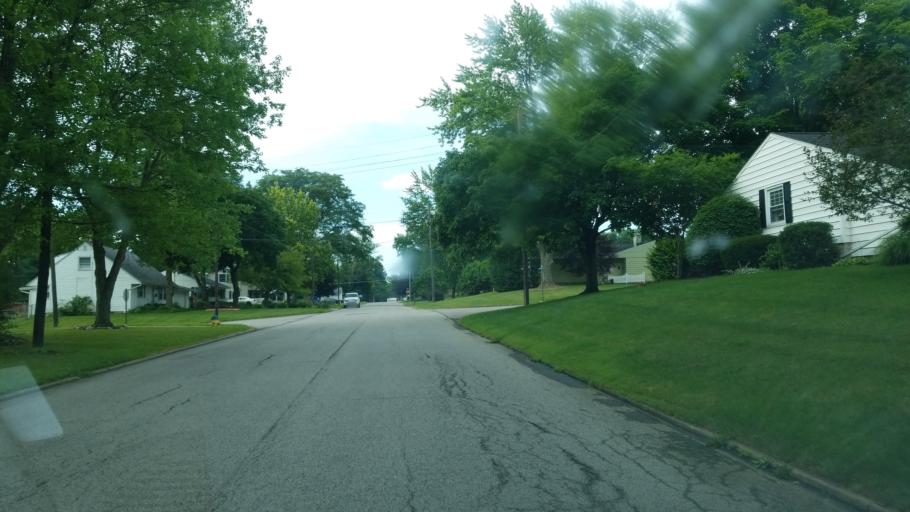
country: US
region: Ohio
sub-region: Ashland County
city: Ashland
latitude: 40.8599
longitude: -82.2990
